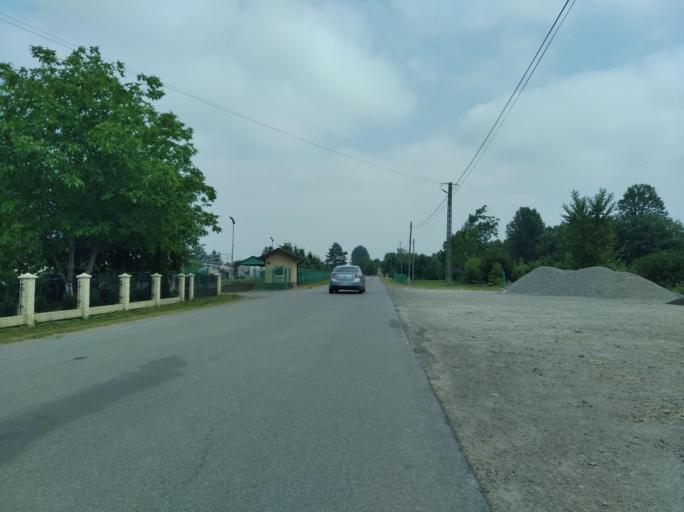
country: PL
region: Subcarpathian Voivodeship
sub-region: Powiat sanocki
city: Besko
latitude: 49.5939
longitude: 21.9604
